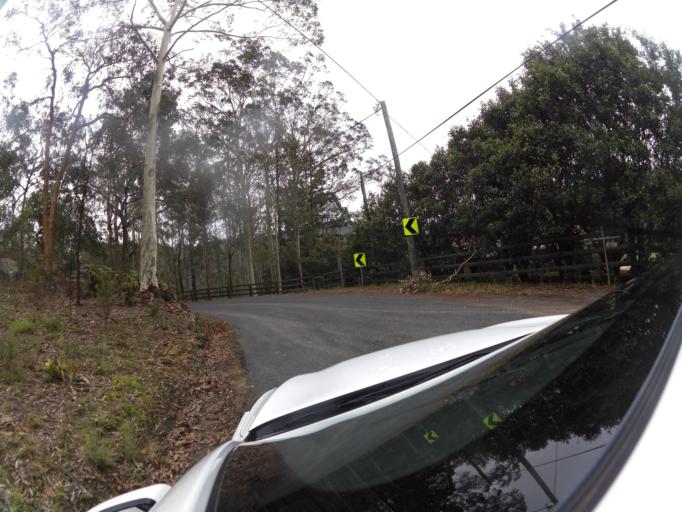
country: AU
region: New South Wales
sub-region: Hawkesbury
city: Pitt Town
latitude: -33.4189
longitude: 150.9371
